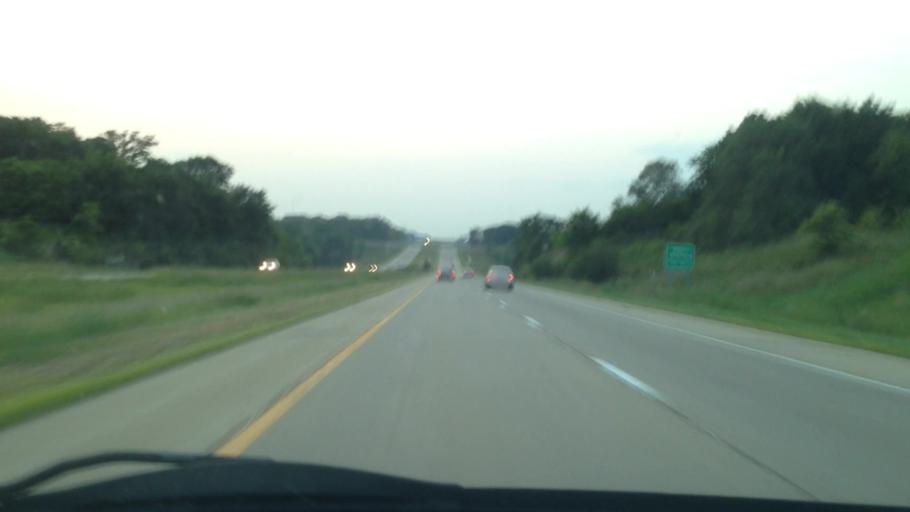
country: US
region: Iowa
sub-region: Benton County
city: Urbana
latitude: 42.3163
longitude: -91.9827
